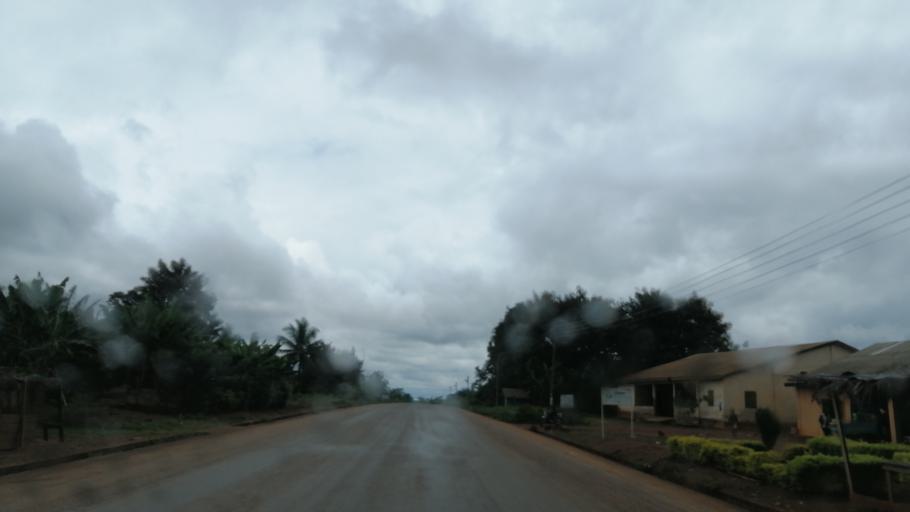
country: GH
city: Duayaw Nkwanta
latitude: 6.9126
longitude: -2.3893
